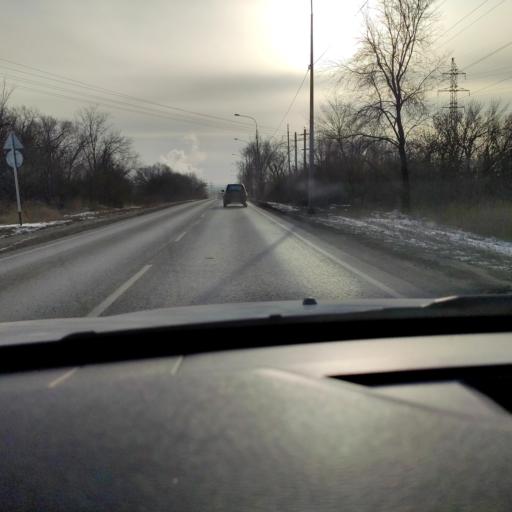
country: RU
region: Samara
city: Petra-Dubrava
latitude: 53.2744
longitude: 50.3826
